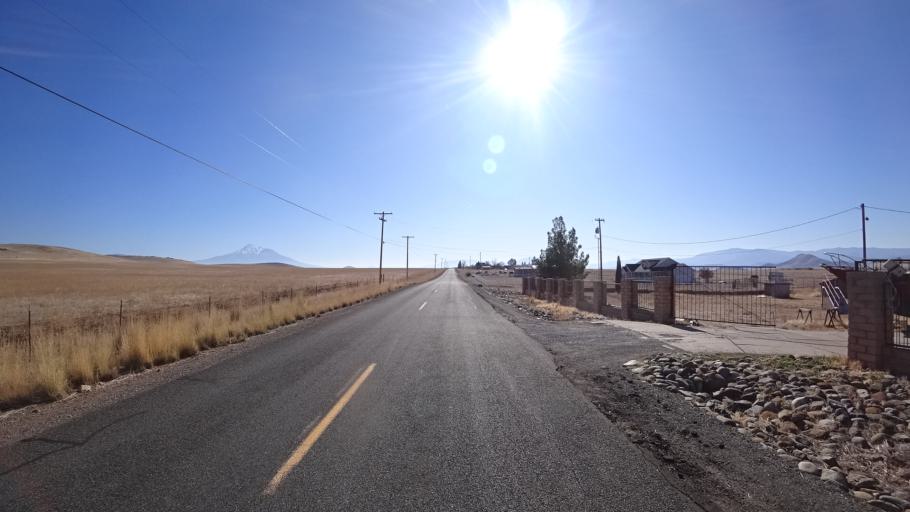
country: US
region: California
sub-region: Siskiyou County
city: Montague
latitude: 41.7507
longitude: -122.4572
